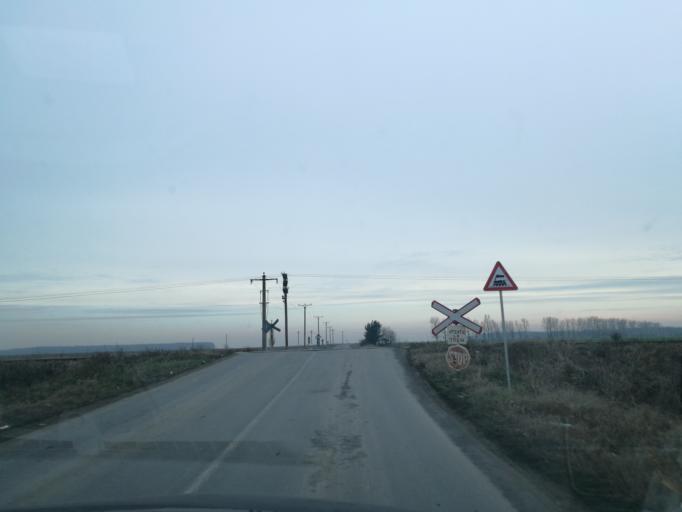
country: RO
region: Ilfov
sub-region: Comuna Gradistea
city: Gradistea
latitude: 44.6541
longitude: 26.3037
